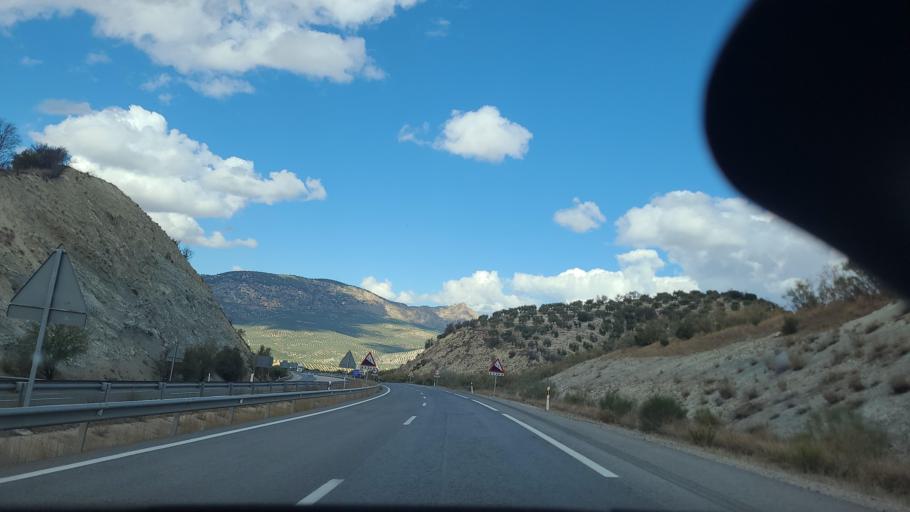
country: ES
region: Andalusia
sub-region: Provincia de Jaen
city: Campillo de Arenas
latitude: 37.5417
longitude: -3.6349
